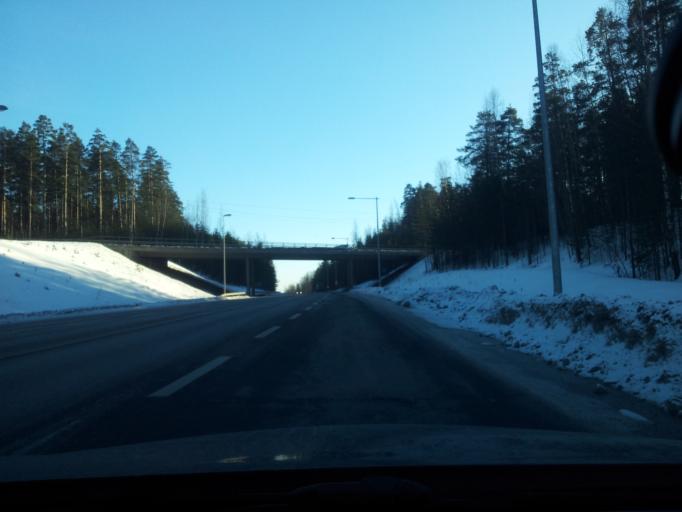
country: FI
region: Uusimaa
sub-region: Helsinki
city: Vihti
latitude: 60.3520
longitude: 24.3290
